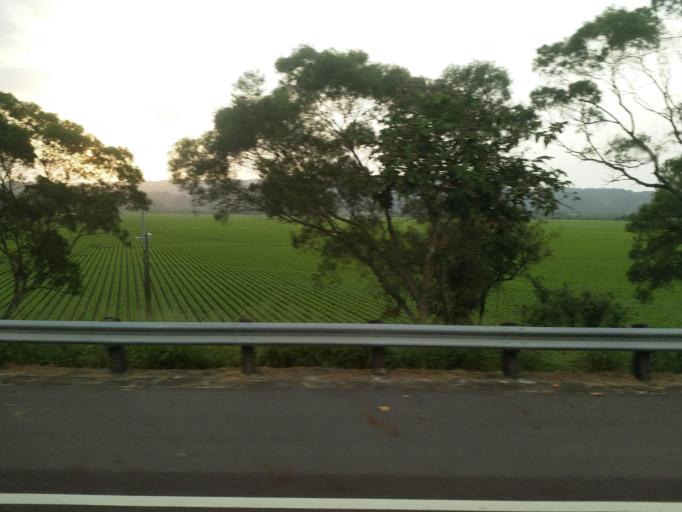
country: TW
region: Taiwan
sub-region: Pingtung
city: Pingtung
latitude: 22.8242
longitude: 120.4878
